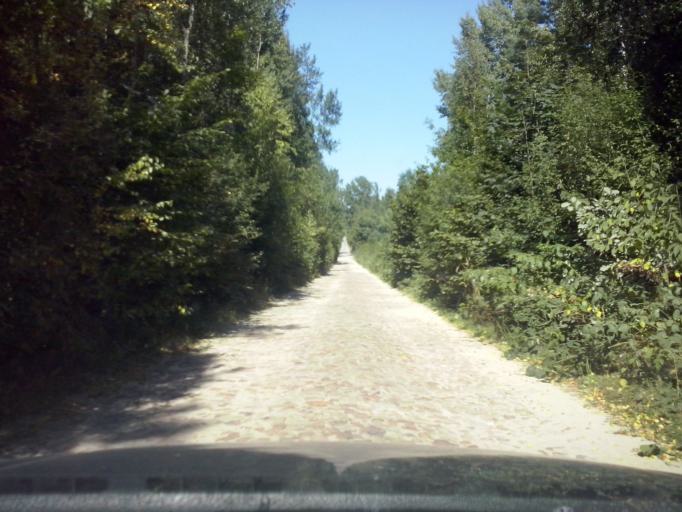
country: PL
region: Swietokrzyskie
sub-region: Powiat kielecki
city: Bieliny
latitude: 50.7933
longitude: 20.9404
